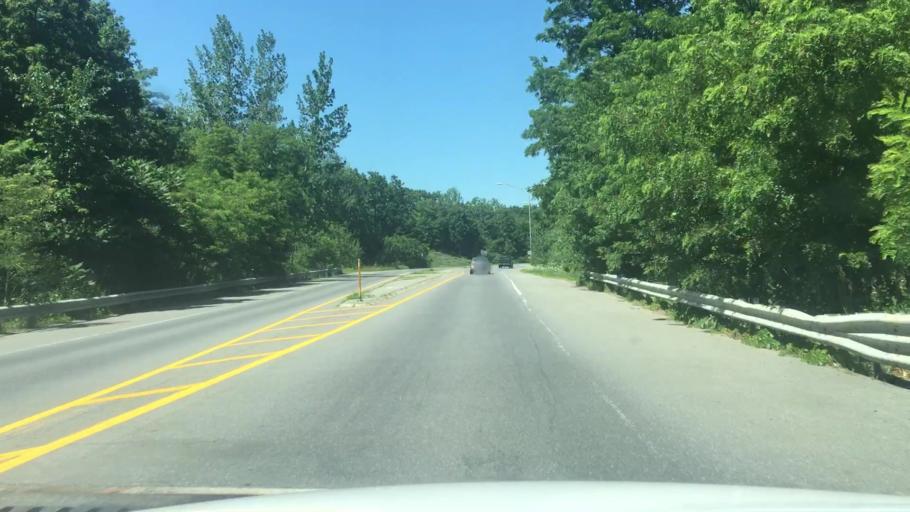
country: US
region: Maine
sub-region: Kennebec County
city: Waterville
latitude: 44.5322
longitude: -69.6486
